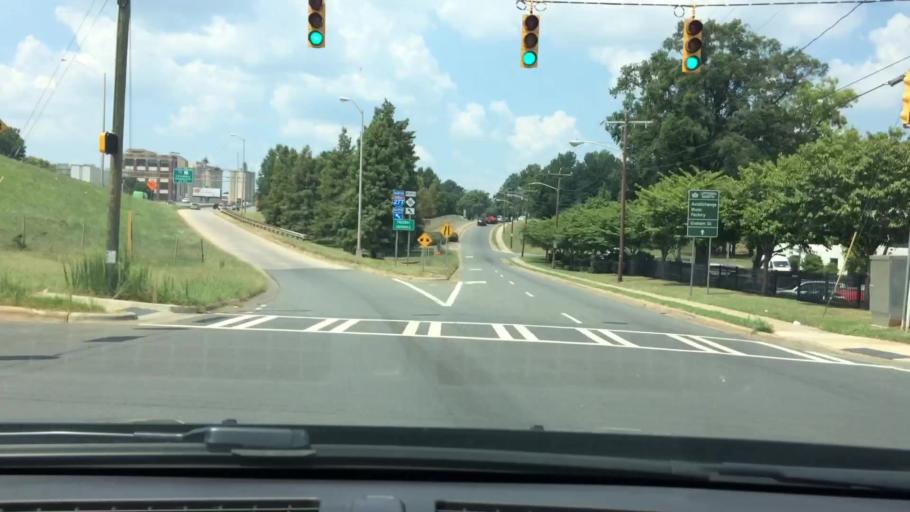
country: US
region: North Carolina
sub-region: Mecklenburg County
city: Charlotte
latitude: 35.2342
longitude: -80.8356
